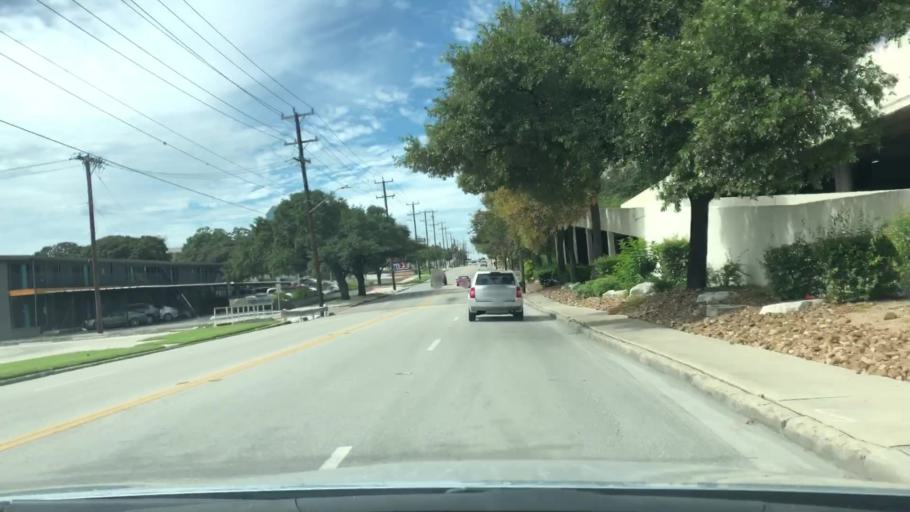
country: US
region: Texas
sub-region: Bexar County
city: Castle Hills
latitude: 29.5169
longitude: -98.4927
